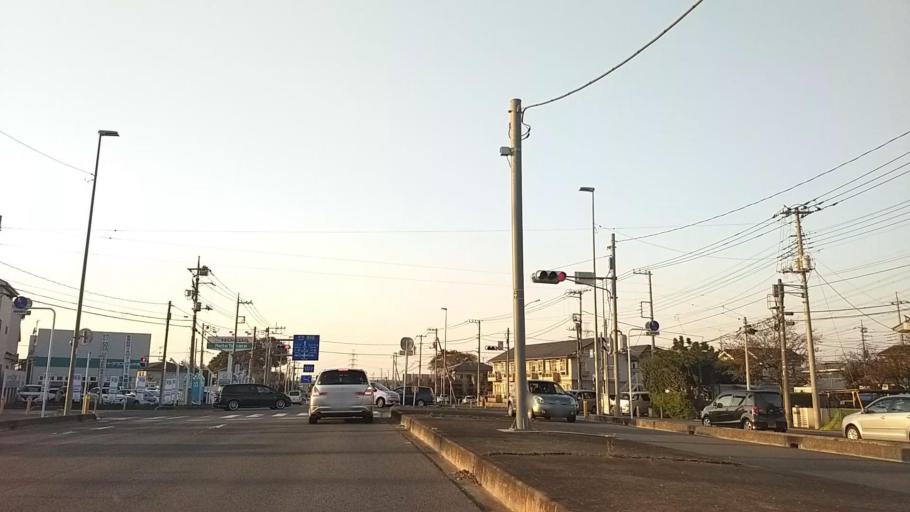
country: JP
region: Saitama
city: Sayama
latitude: 35.8685
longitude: 139.4227
